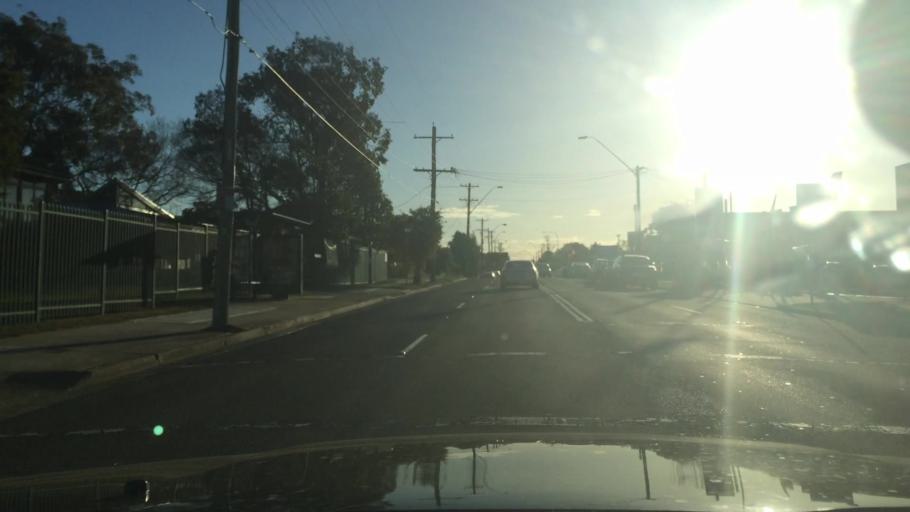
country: AU
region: New South Wales
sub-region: Fairfield
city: Fairfield Heights
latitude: -33.8526
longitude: 150.9343
